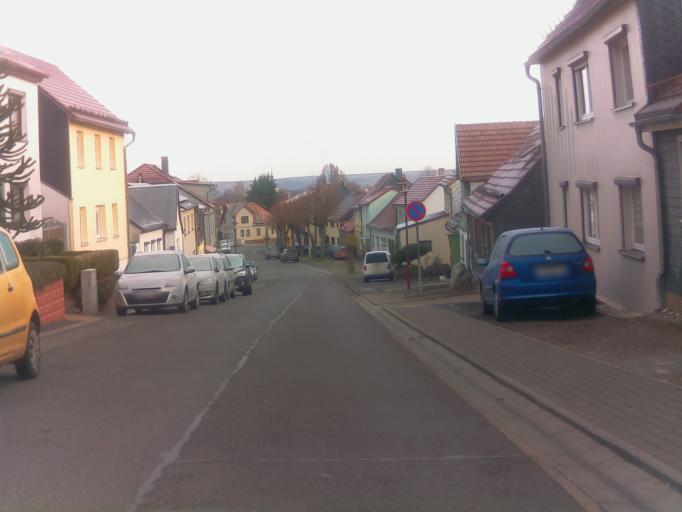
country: DE
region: Thuringia
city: Grafenhain
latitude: 50.8152
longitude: 10.6953
